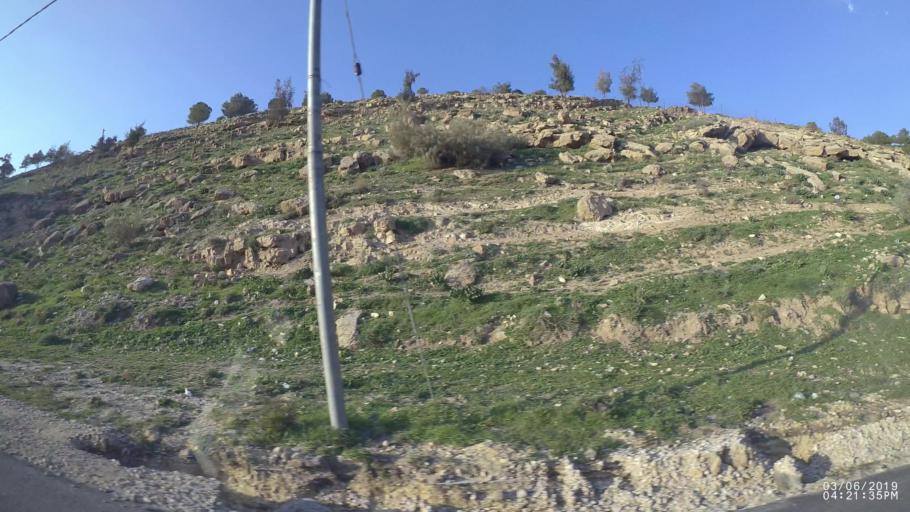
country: JO
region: Amman
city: Amman
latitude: 31.9815
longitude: 35.9655
